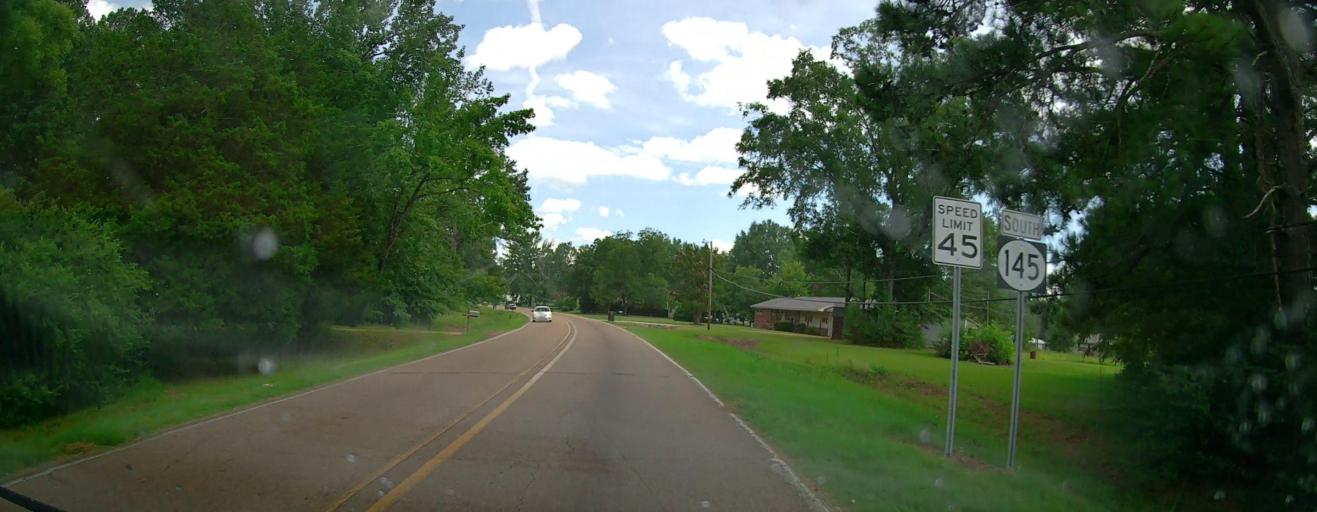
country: US
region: Mississippi
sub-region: Lee County
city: Shannon
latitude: 34.1243
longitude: -88.7180
